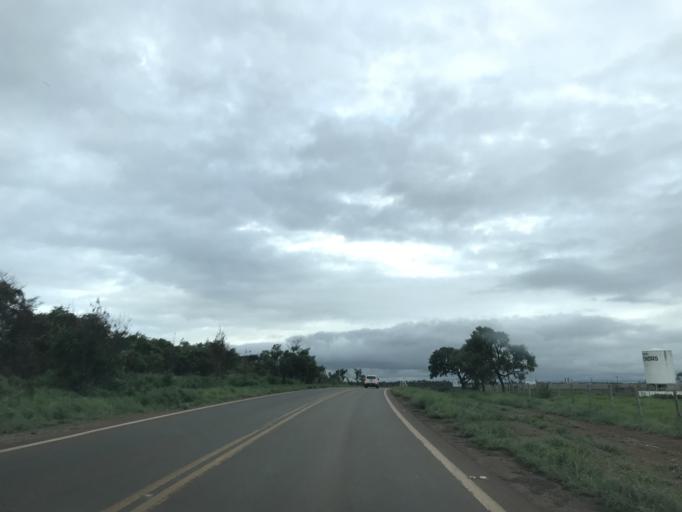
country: BR
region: Goias
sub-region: Luziania
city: Luziania
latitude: -16.2754
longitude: -47.9928
